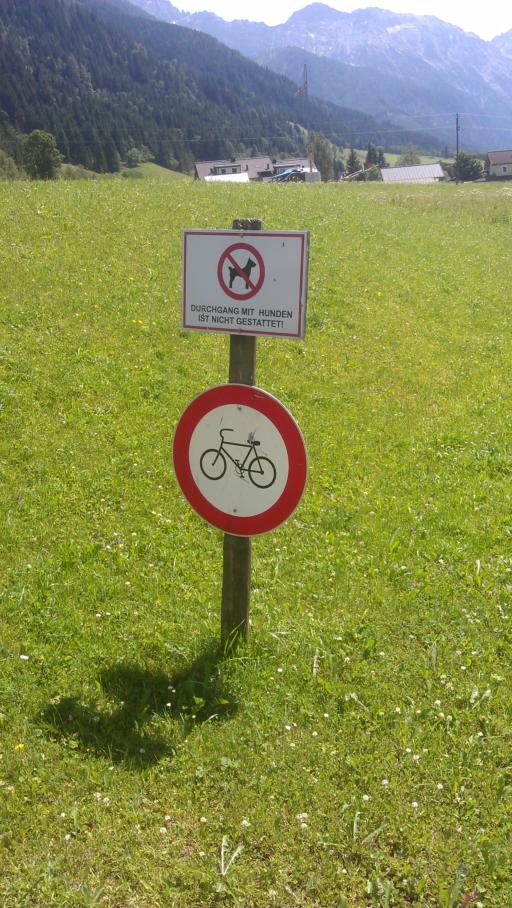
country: AT
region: Salzburg
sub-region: Politischer Bezirk Sankt Johann im Pongau
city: Kleinarl
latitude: 47.2758
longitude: 13.3213
